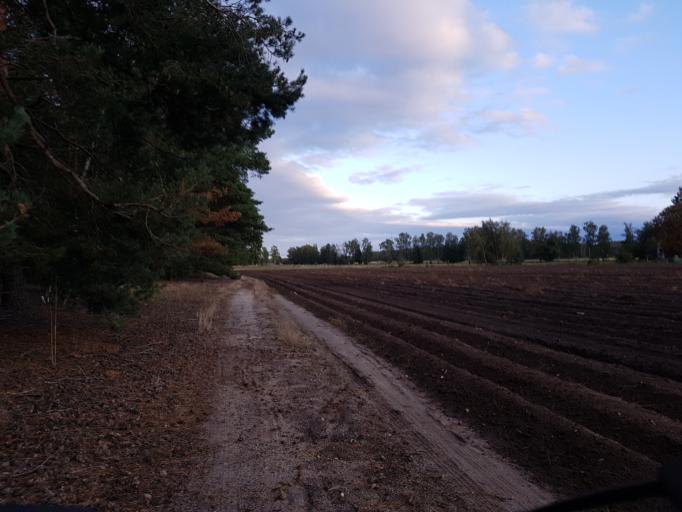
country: DE
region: Brandenburg
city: Schilda
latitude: 51.5951
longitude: 13.3630
